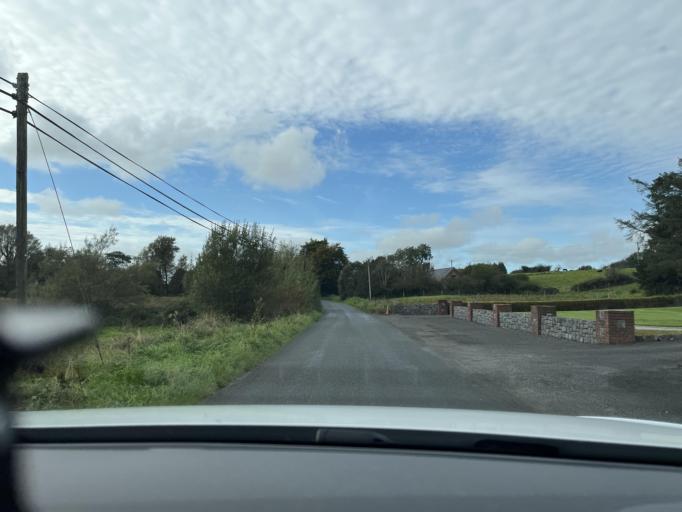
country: IE
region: Connaught
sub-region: Roscommon
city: Boyle
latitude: 54.0236
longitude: -8.3922
